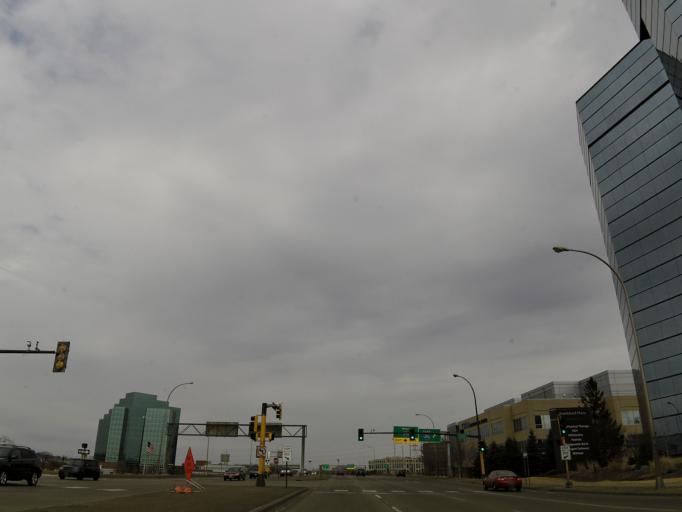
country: US
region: Minnesota
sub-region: Hennepin County
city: Bloomington
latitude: 44.8567
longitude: -93.3290
